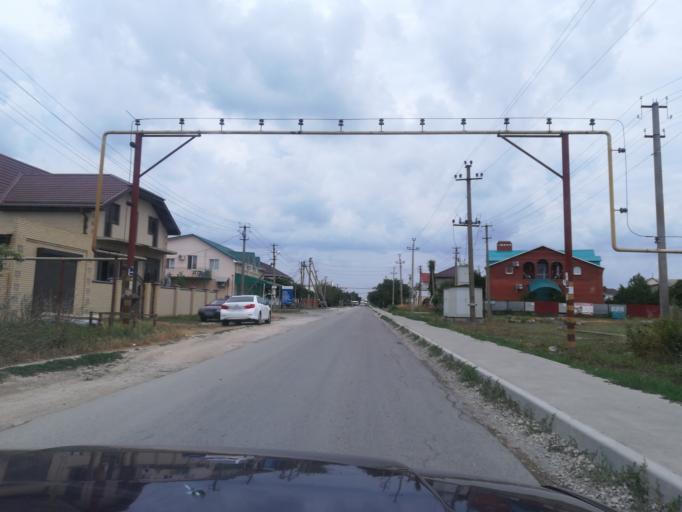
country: RU
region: Krasnodarskiy
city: Vityazevo
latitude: 45.0083
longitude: 37.2889
